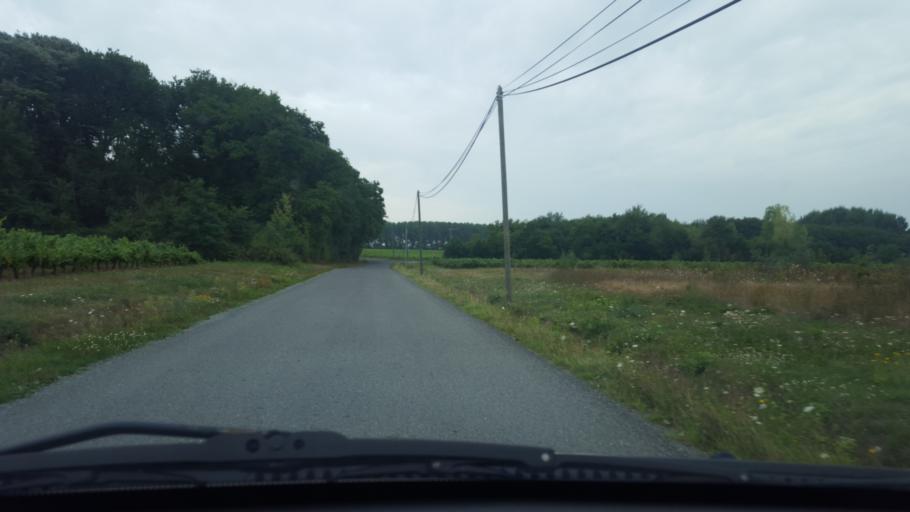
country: FR
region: Pays de la Loire
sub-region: Departement de la Loire-Atlantique
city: Saint-Philbert-de-Grand-Lieu
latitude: 47.0184
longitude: -1.6326
